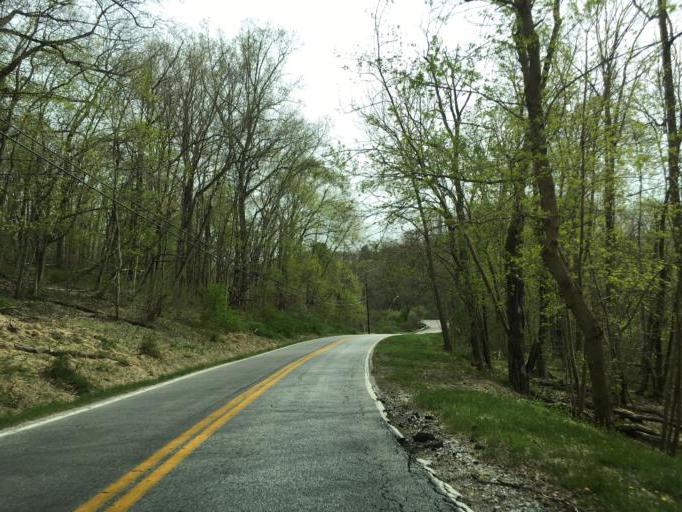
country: US
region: Maryland
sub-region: Baltimore County
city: Hunt Valley
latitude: 39.5203
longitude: -76.6174
